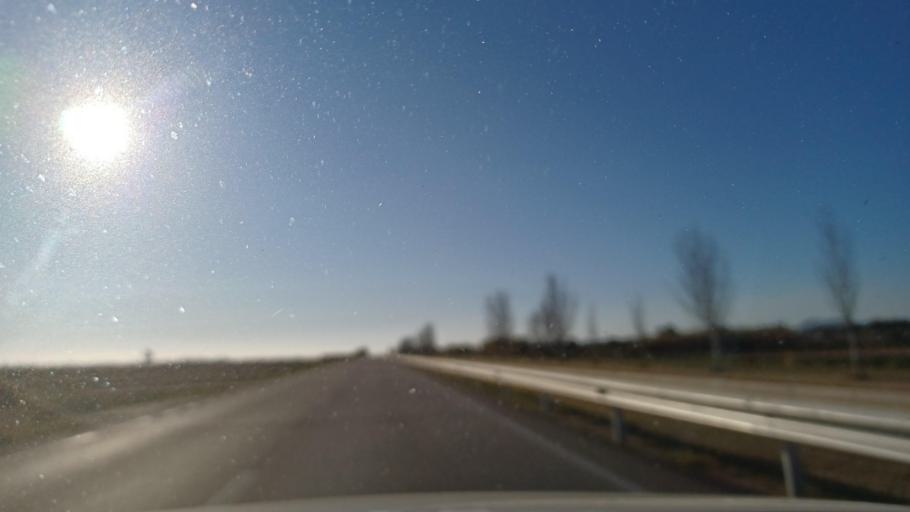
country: ES
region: Catalonia
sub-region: Provincia de Tarragona
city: Sant Carles de la Rapita
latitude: 40.6533
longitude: 0.5954
